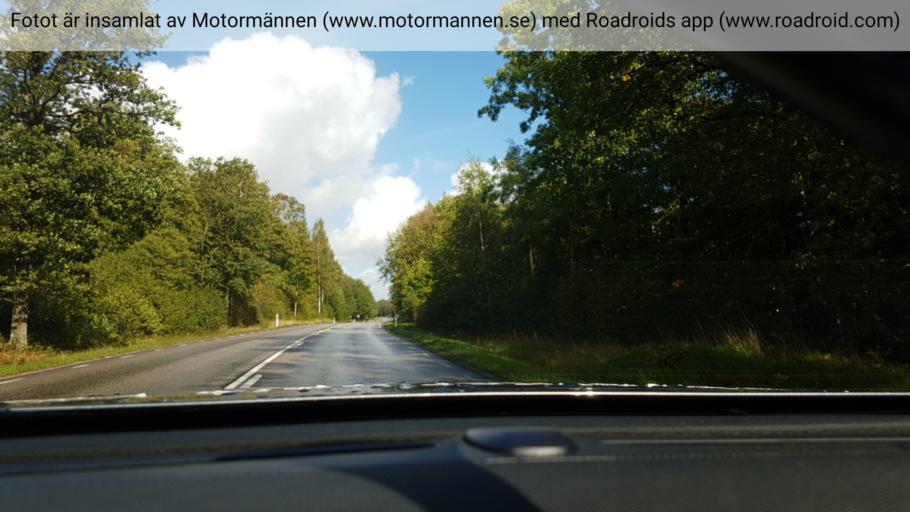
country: SE
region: Vaestra Goetaland
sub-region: Alingsas Kommun
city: Sollebrunn
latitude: 58.0612
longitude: 12.4685
